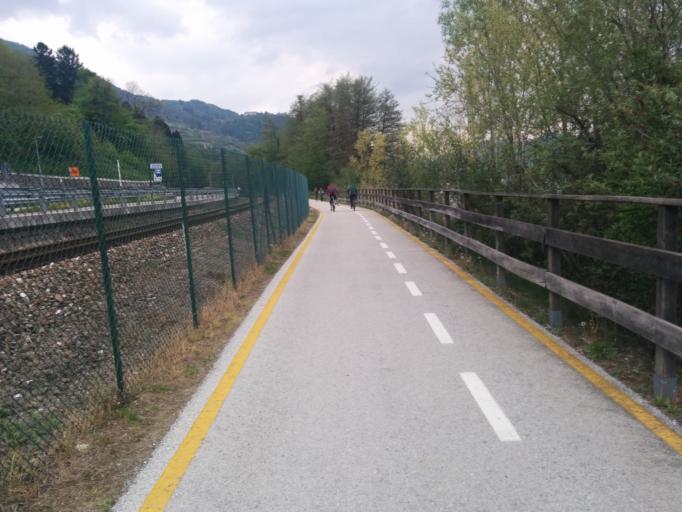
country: IT
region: Trentino-Alto Adige
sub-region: Provincia di Trento
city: Calceranica al Lago
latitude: 46.0159
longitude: 11.2347
